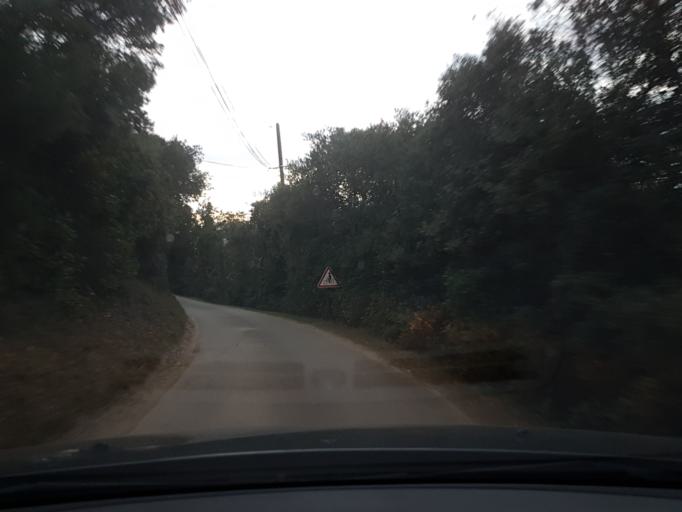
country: FR
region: Provence-Alpes-Cote d'Azur
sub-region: Departement du Vaucluse
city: Loriol-du-Comtat
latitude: 44.0887
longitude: 4.9968
